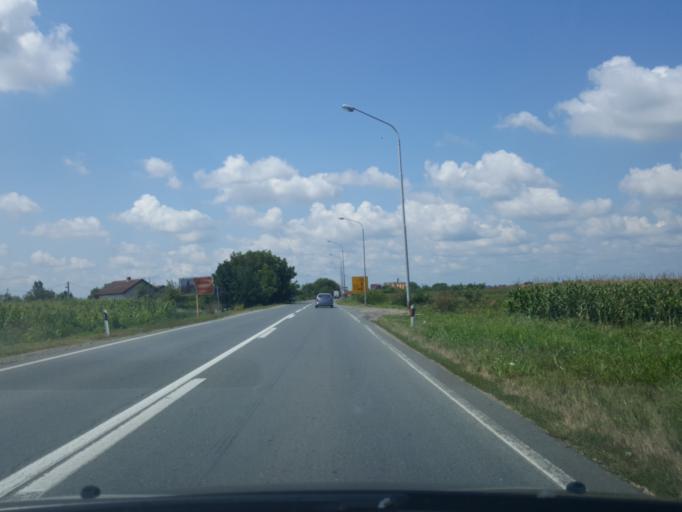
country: RS
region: Autonomna Pokrajina Vojvodina
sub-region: Sremski Okrug
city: Sremska Mitrovica
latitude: 44.9515
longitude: 19.6265
